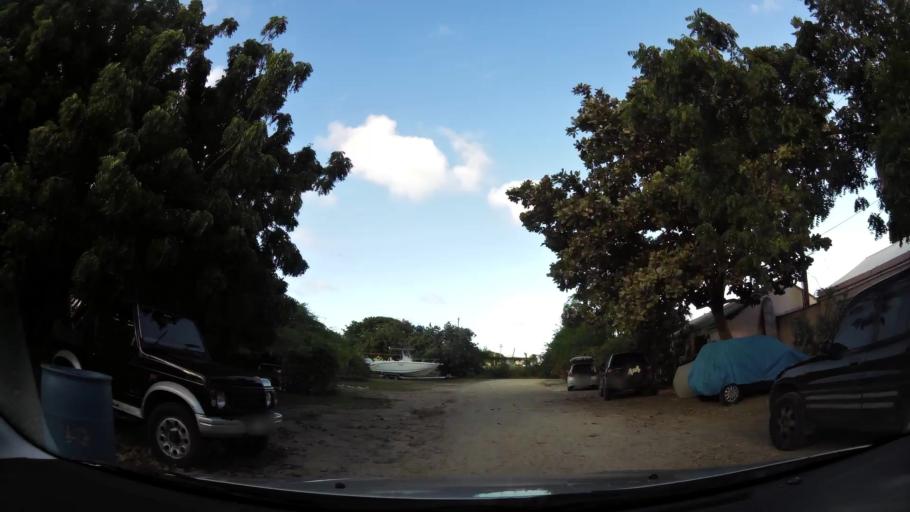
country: AG
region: Saint George
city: Piggotts
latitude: 17.1548
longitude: -61.7915
